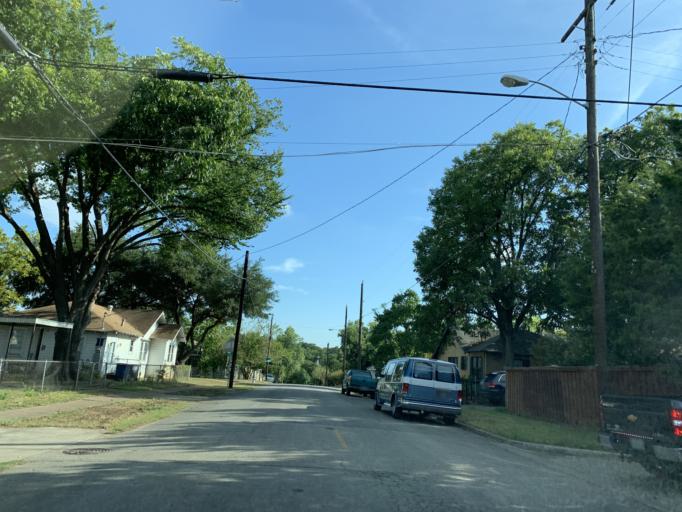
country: US
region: Texas
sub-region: Dallas County
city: Dallas
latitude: 32.7369
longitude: -96.8322
